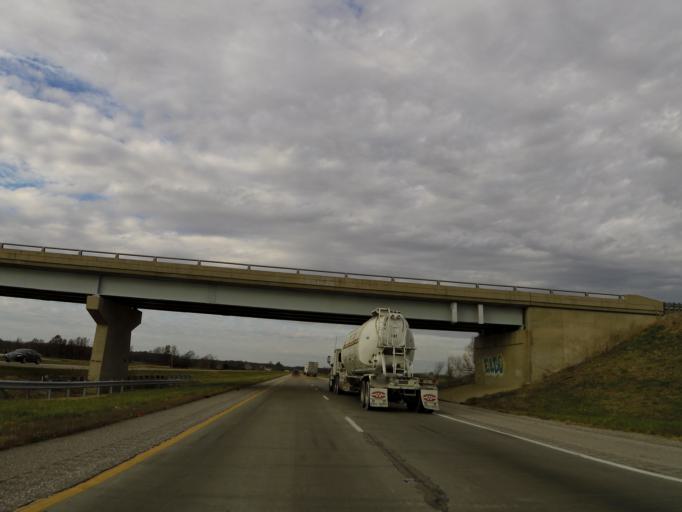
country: US
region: Illinois
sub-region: Washington County
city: Nashville
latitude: 38.3912
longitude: -89.2746
